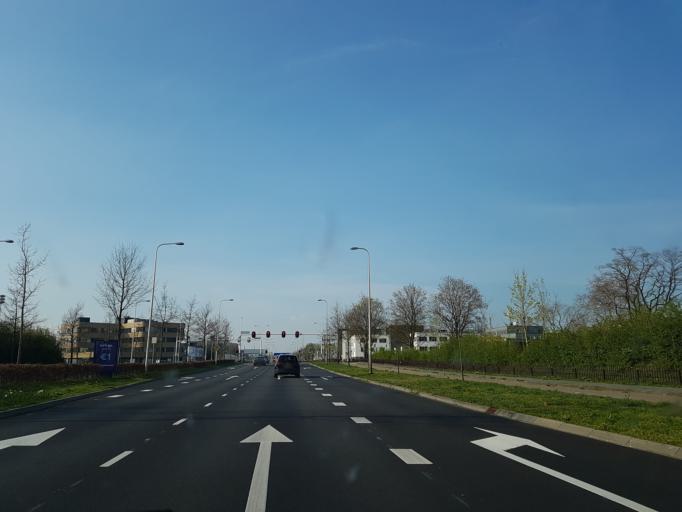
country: NL
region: Overijssel
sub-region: Gemeente Zwolle
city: Zwolle
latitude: 52.5127
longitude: 6.1207
